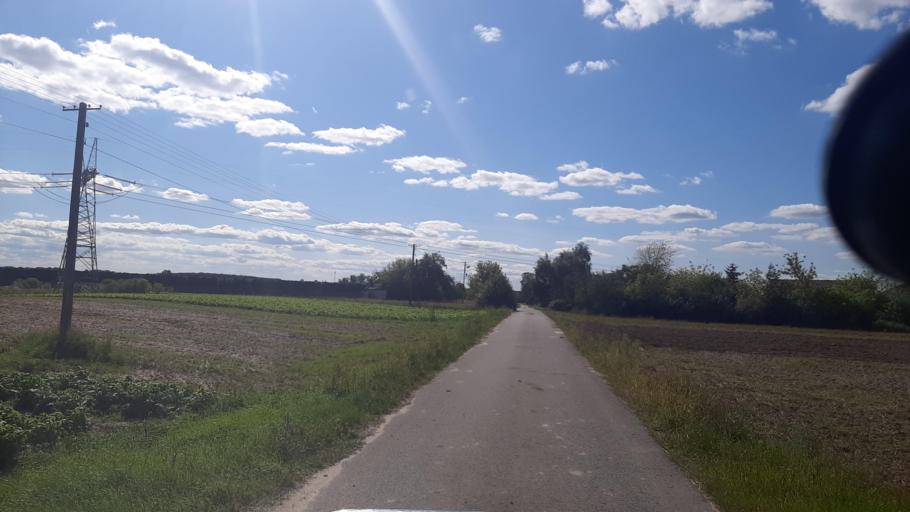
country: PL
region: Lublin Voivodeship
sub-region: Powiat pulawski
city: Markuszow
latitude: 51.3966
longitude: 22.2311
